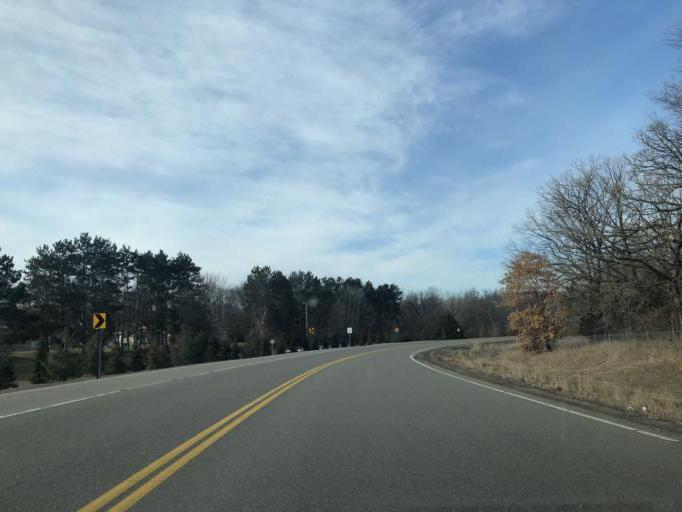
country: US
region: Minnesota
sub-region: Sherburne County
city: Becker
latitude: 45.3953
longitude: -93.8502
